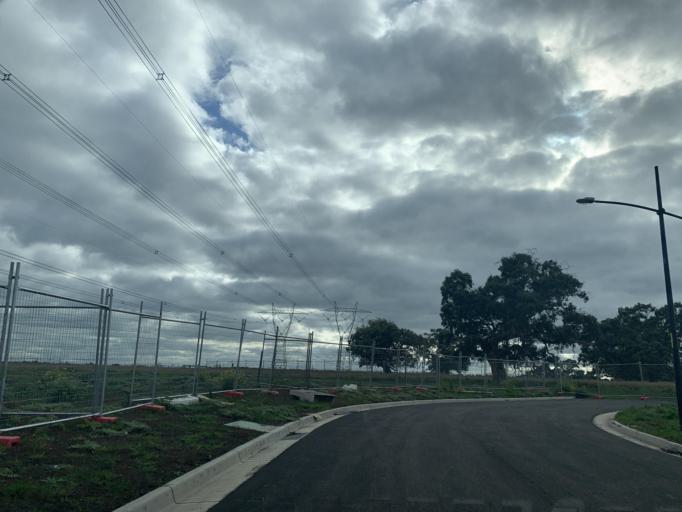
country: AU
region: Victoria
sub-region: Hume
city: Craigieburn
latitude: -37.5968
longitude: 145.0070
